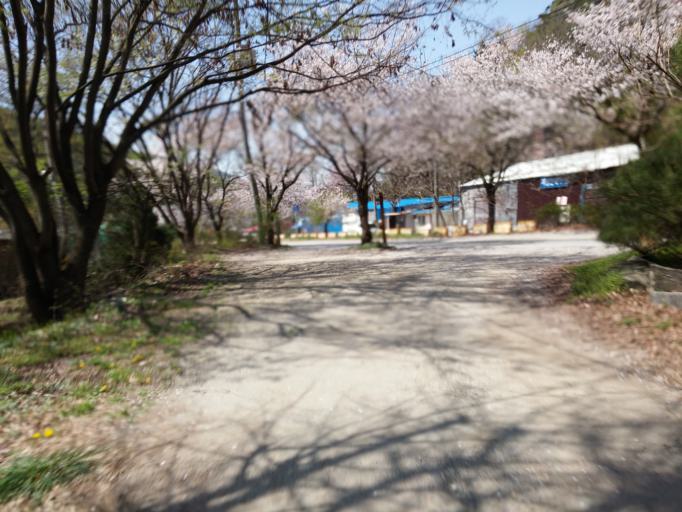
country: KR
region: Daejeon
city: Daejeon
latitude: 36.2800
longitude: 127.4759
